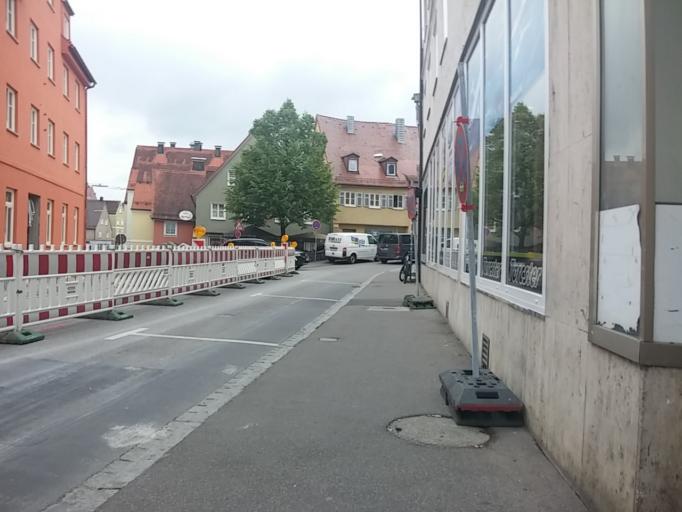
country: DE
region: Bavaria
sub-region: Swabia
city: Memmingen
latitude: 47.9836
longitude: 10.1795
